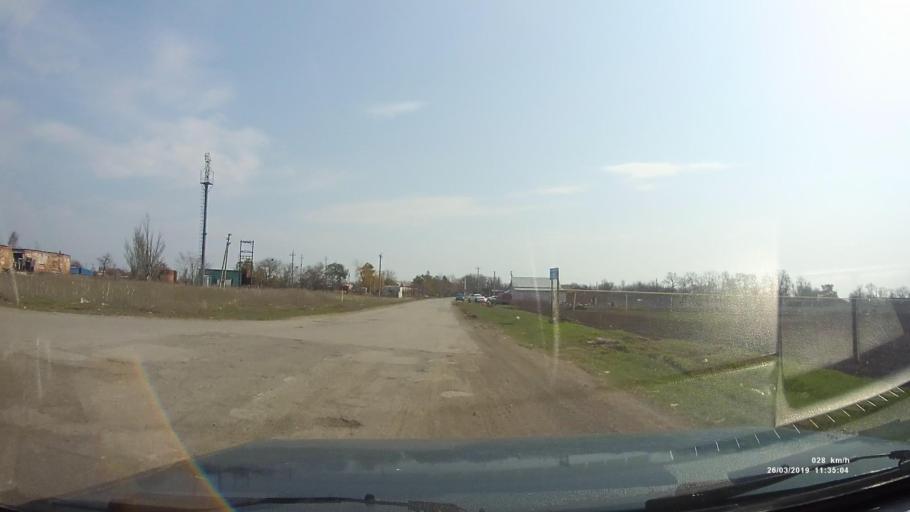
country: RU
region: Rostov
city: Novobessergenovka
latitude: 47.1471
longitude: 38.6353
